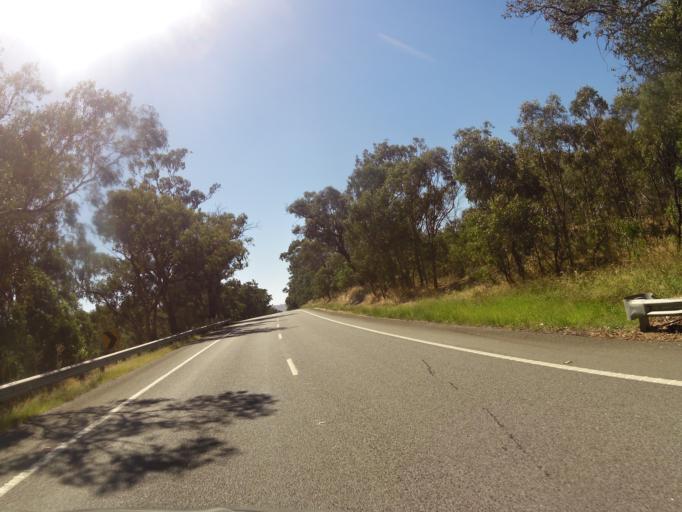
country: AU
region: Victoria
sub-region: Greater Shepparton
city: Shepparton
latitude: -36.7707
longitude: 145.5237
